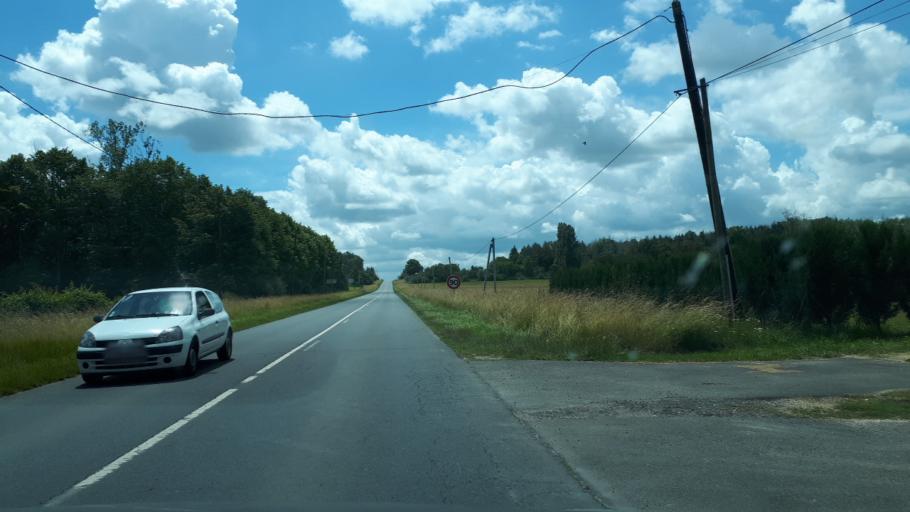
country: FR
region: Centre
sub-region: Departement du Loir-et-Cher
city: Contres
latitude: 47.4088
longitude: 1.4215
